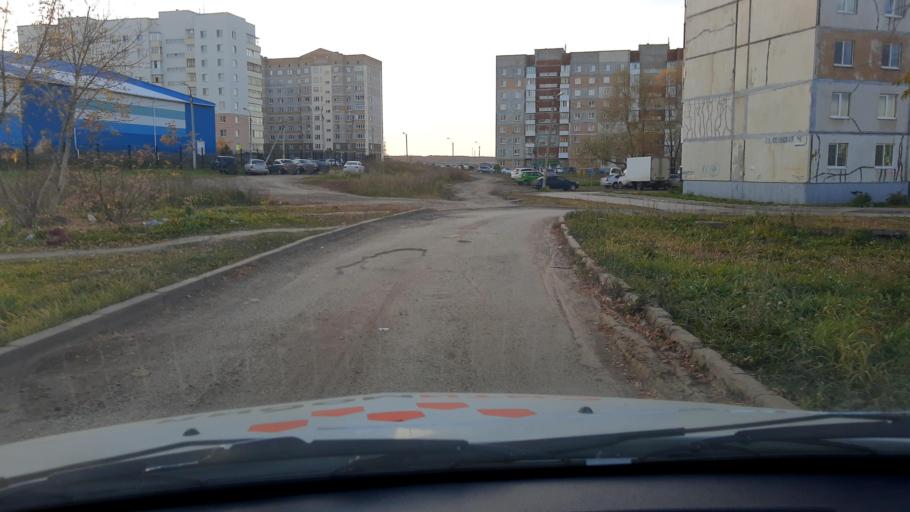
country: RU
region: Bashkortostan
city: Iglino
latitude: 54.7564
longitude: 56.2419
